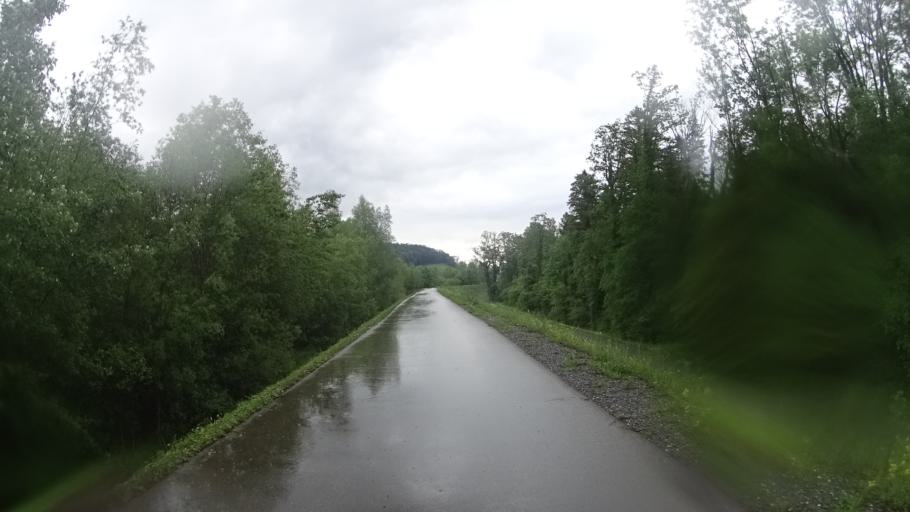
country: AT
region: Vorarlberg
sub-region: Politischer Bezirk Feldkirch
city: Meiningen
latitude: 47.2962
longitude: 9.5588
